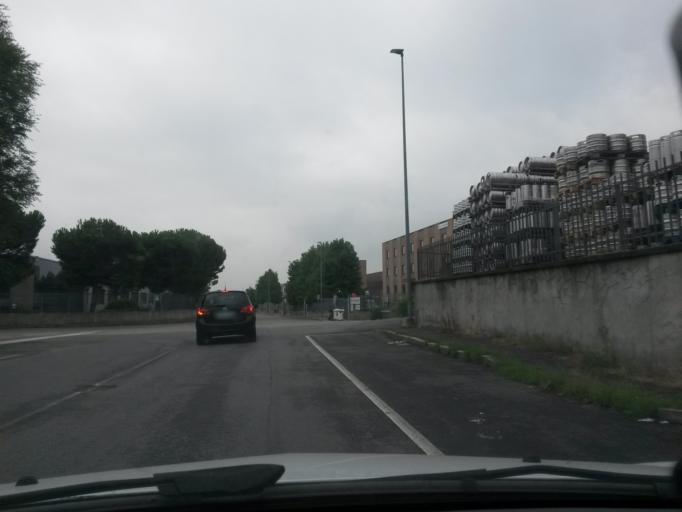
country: IT
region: Piedmont
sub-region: Provincia di Torino
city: Rivoli
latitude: 45.0649
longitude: 7.5361
